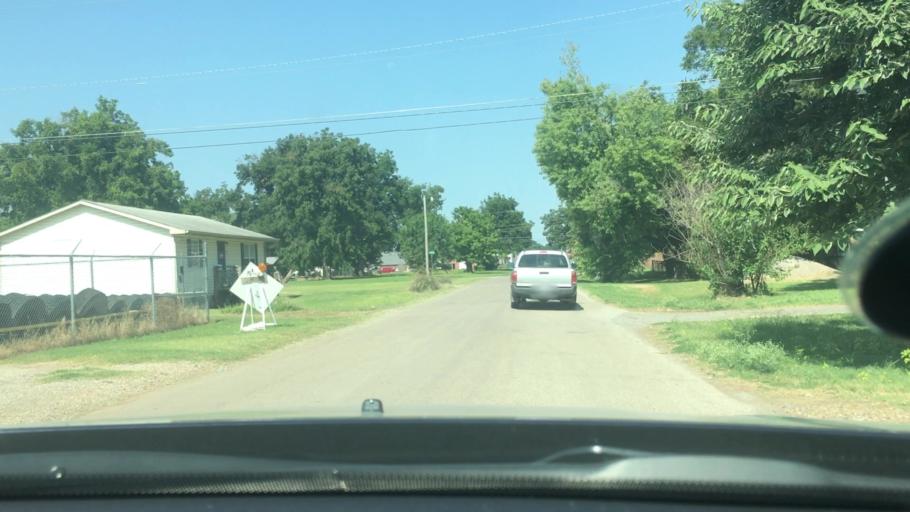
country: US
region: Oklahoma
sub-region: Garvin County
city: Lindsay
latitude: 34.8336
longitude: -97.5989
